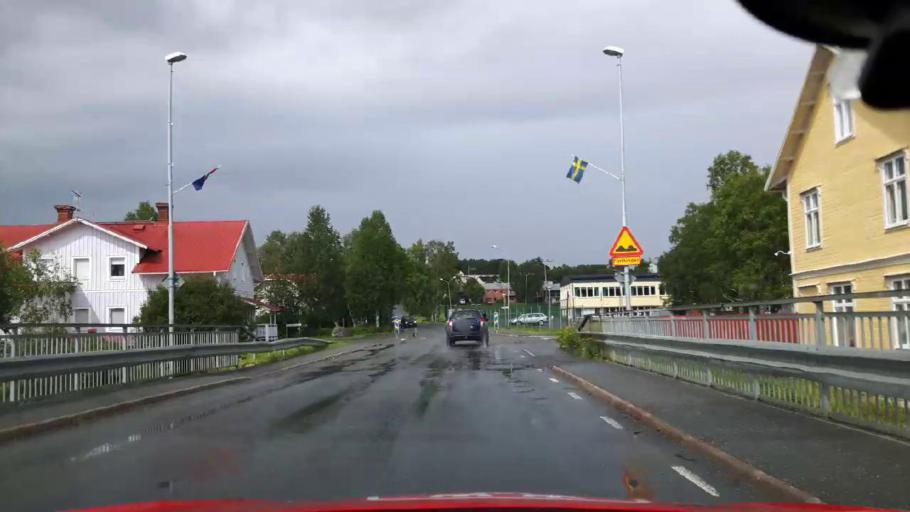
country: SE
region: Jaemtland
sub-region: Krokoms Kommun
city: Krokom
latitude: 63.3495
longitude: 14.2518
